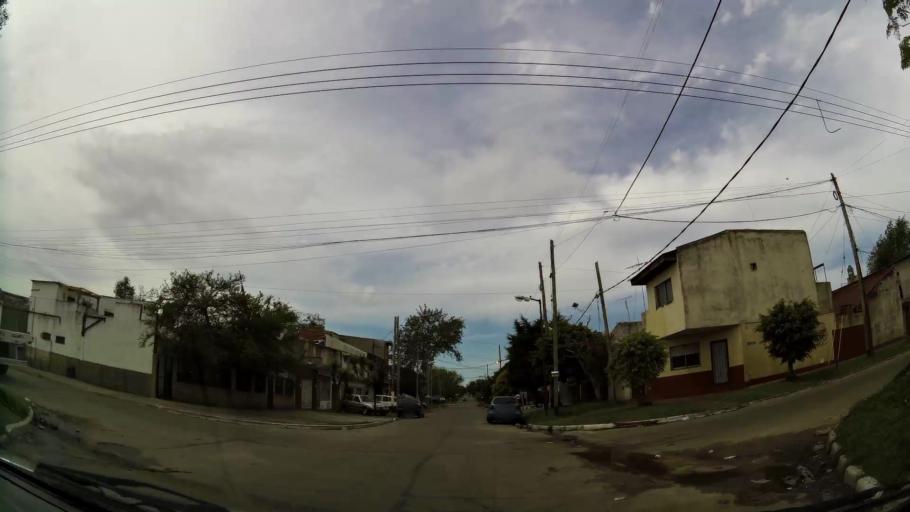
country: AR
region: Buenos Aires
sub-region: Partido de Quilmes
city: Quilmes
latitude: -34.7601
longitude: -58.2652
